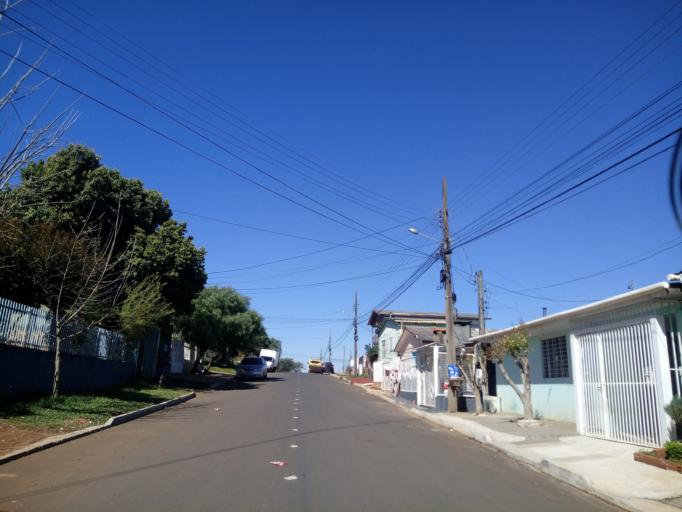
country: BR
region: Santa Catarina
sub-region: Chapeco
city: Chapeco
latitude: -27.0972
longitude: -52.6808
